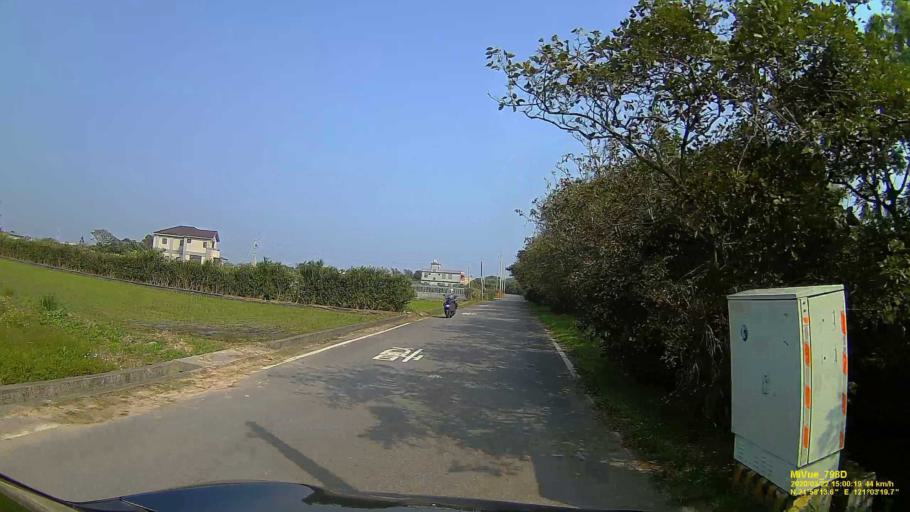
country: TW
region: Taiwan
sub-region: Hsinchu
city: Zhubei
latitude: 24.9703
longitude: 121.0558
